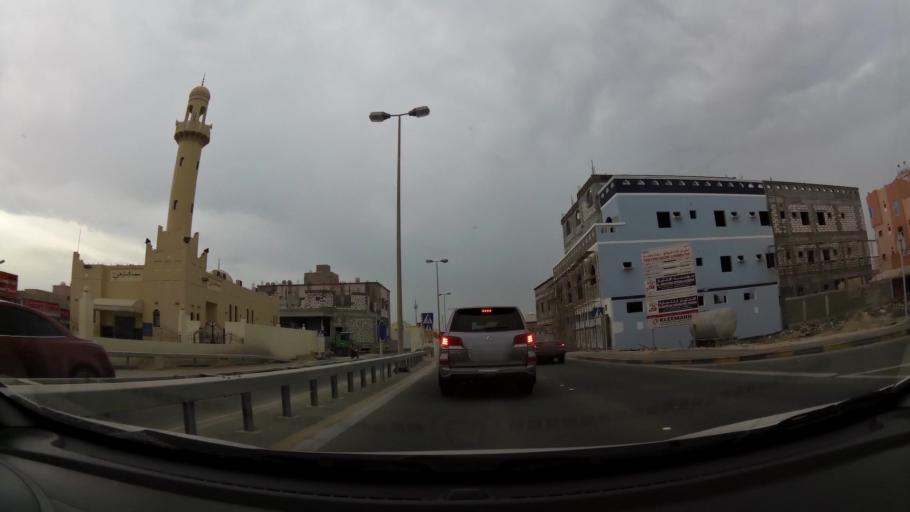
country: BH
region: Central Governorate
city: Madinat Hamad
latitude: 26.0962
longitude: 50.4969
